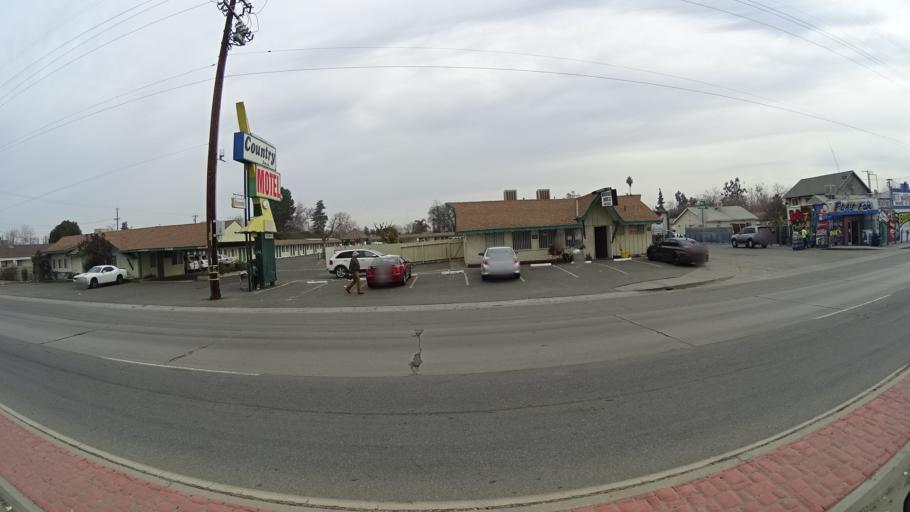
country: US
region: California
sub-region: Kern County
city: Bakersfield
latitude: 35.3439
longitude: -119.0030
